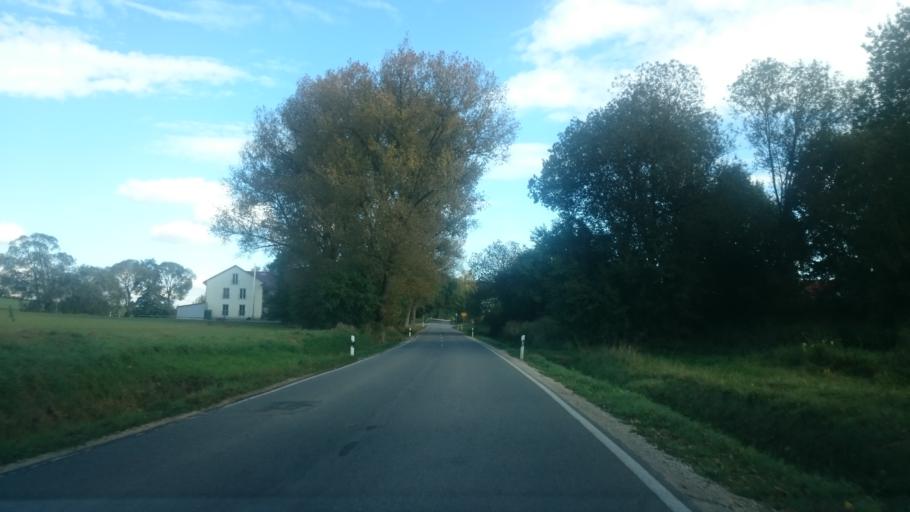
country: DE
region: Bavaria
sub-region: Regierungsbezirk Mittelfranken
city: Hilpoltstein
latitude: 49.1513
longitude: 11.2402
